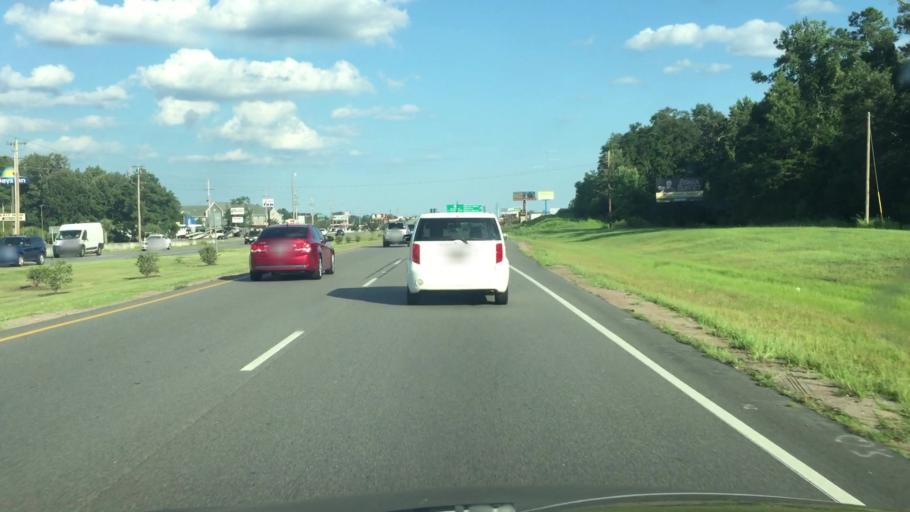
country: US
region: South Carolina
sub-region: Horry County
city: Forestbrook
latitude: 33.7247
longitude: -78.9367
